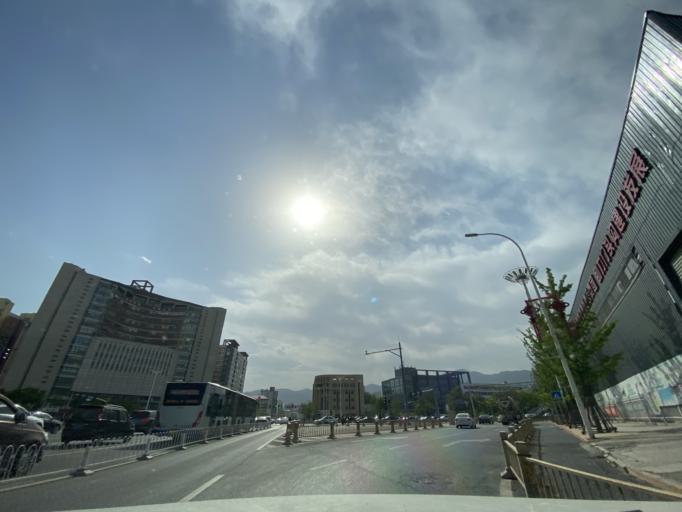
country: CN
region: Beijing
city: Dayu
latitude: 39.9350
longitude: 116.1066
